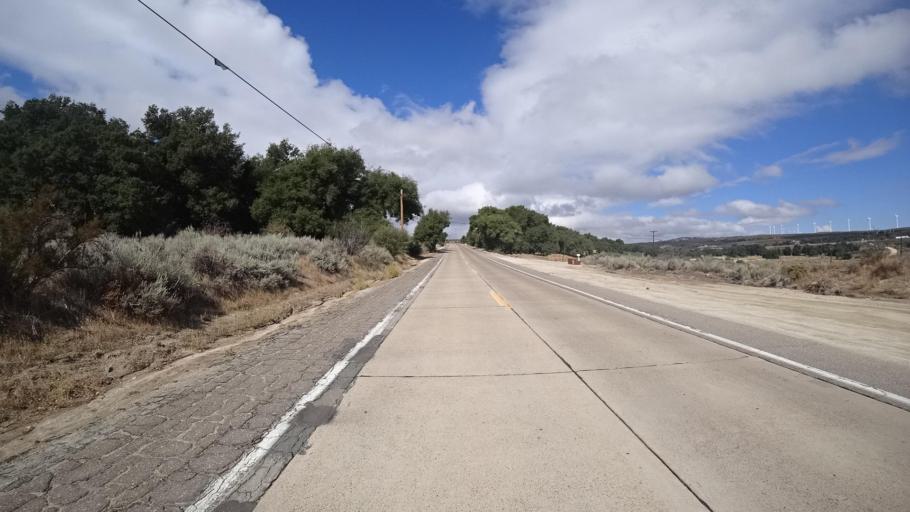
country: US
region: California
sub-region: San Diego County
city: Campo
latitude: 32.6942
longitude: -116.3442
